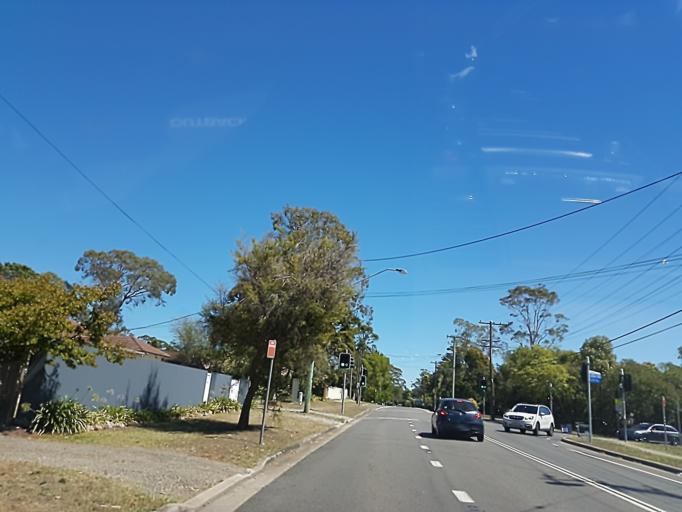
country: AU
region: New South Wales
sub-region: Hornsby Shire
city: Hornsby Heights
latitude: -33.6713
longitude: 151.0963
